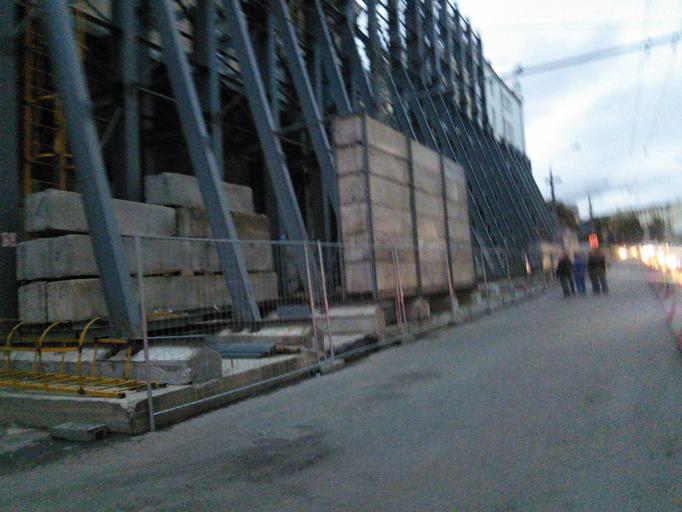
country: RU
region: Moscow
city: Moscow
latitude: 55.7521
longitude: 37.6331
